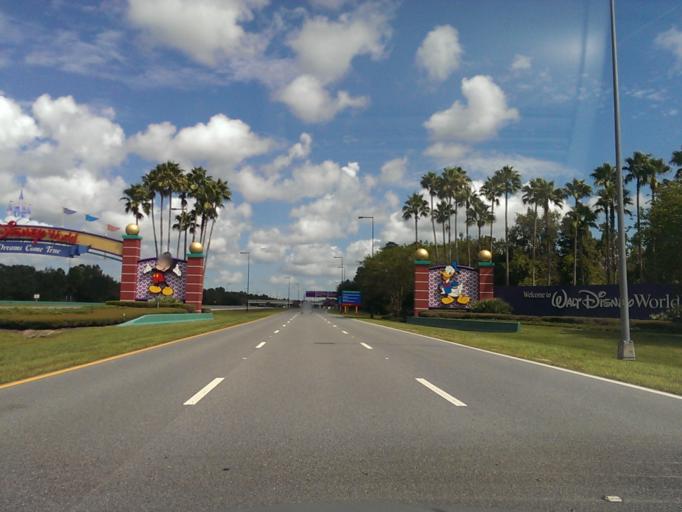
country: US
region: Florida
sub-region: Osceola County
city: Celebration
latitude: 28.3424
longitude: -81.5658
